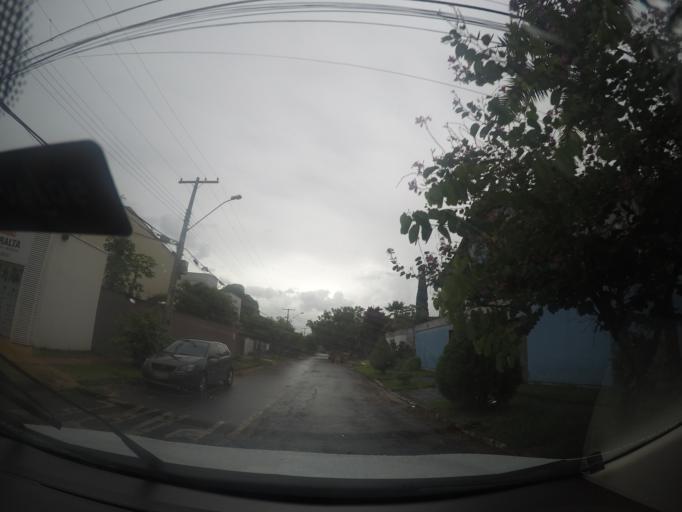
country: BR
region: Goias
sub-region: Goiania
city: Goiania
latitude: -16.6485
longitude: -49.2305
